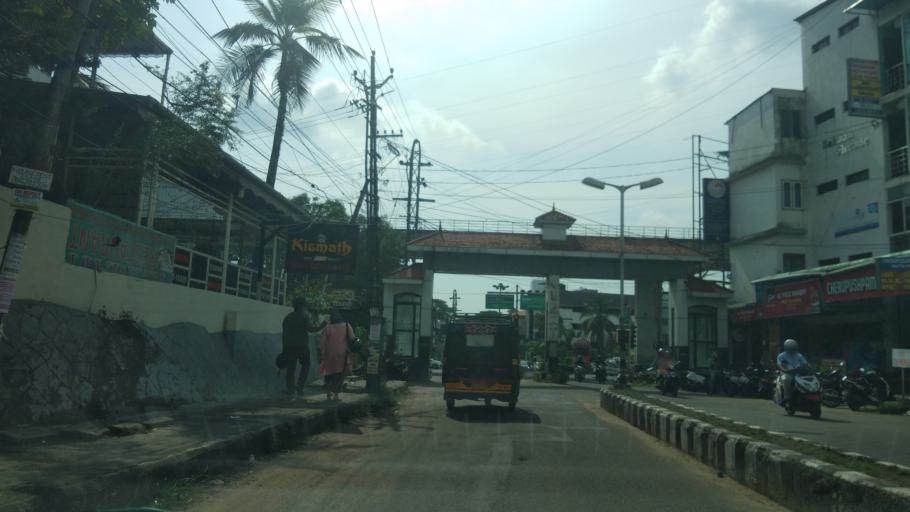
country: IN
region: Kerala
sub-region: Ernakulam
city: Elur
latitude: 10.0474
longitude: 76.3190
